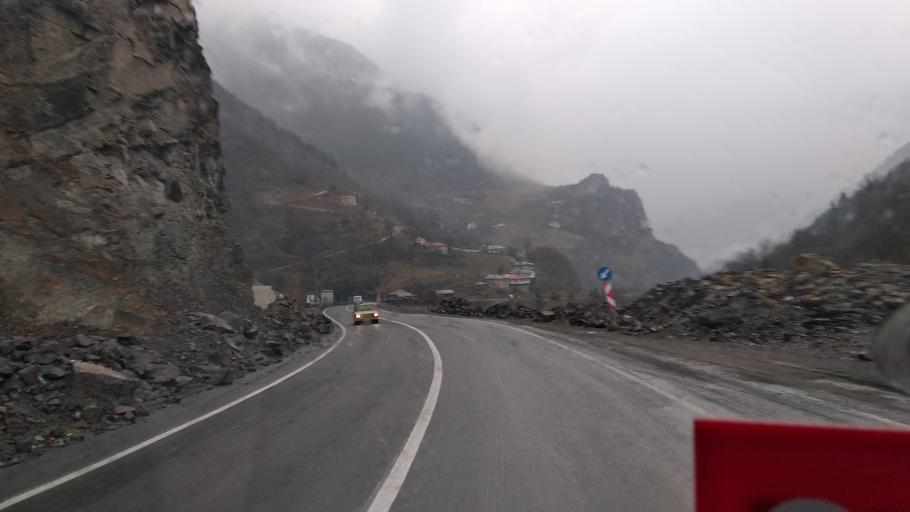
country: TR
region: Trabzon
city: Macka
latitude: 40.7246
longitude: 39.5227
